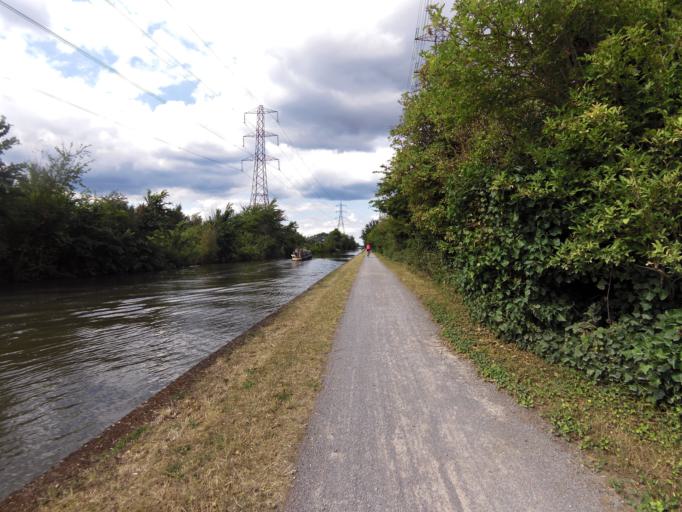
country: GB
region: England
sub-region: Greater London
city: Walthamstow
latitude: 51.6328
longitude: -0.0304
